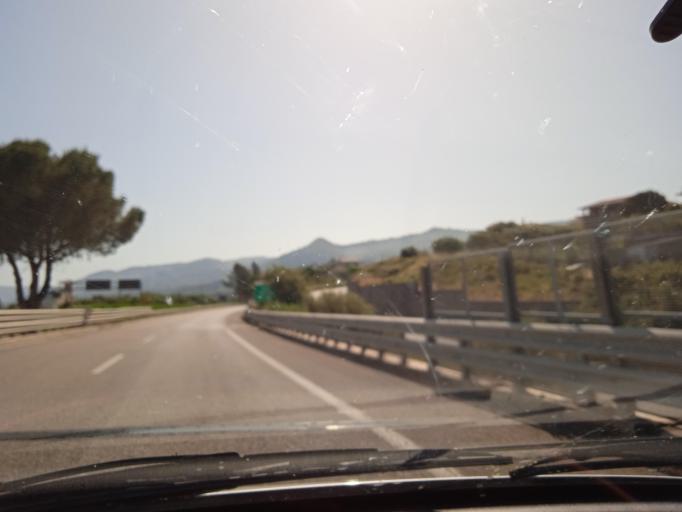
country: IT
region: Sicily
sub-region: Messina
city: Sant'Agata di Militello
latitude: 38.0604
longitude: 14.6263
